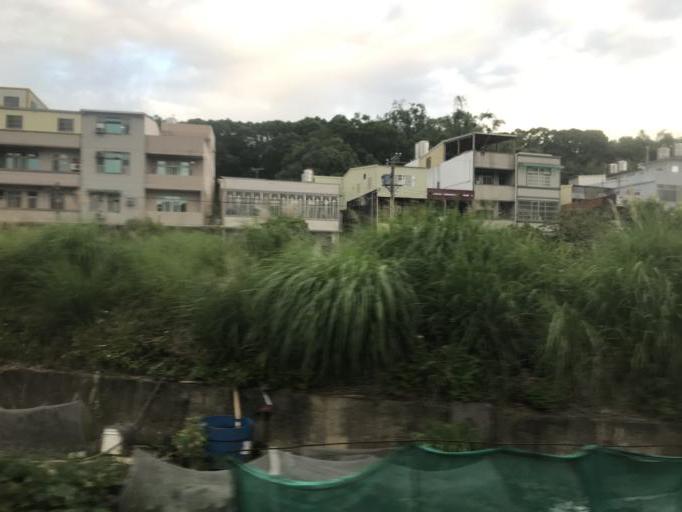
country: TW
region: Taiwan
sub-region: Hsinchu
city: Hsinchu
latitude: 24.7789
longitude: 120.9370
